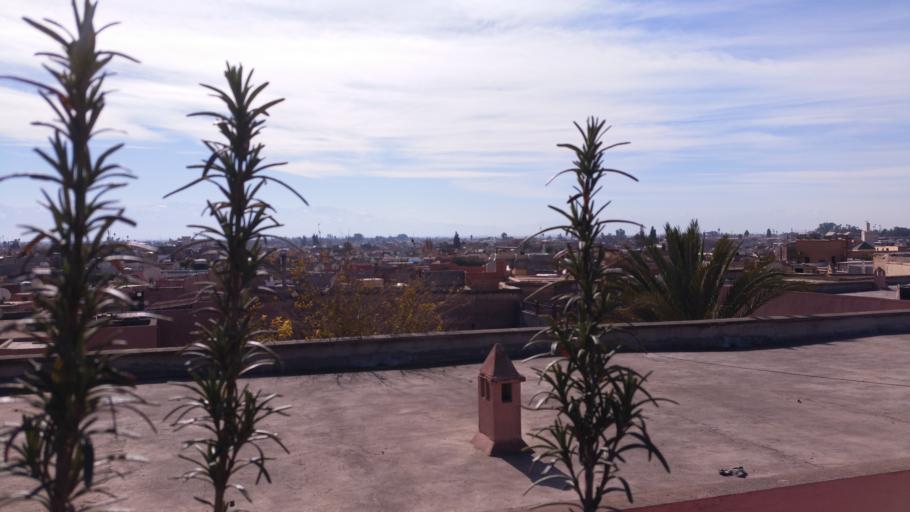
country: MA
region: Marrakech-Tensift-Al Haouz
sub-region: Marrakech
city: Marrakesh
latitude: 31.6320
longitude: -7.9843
